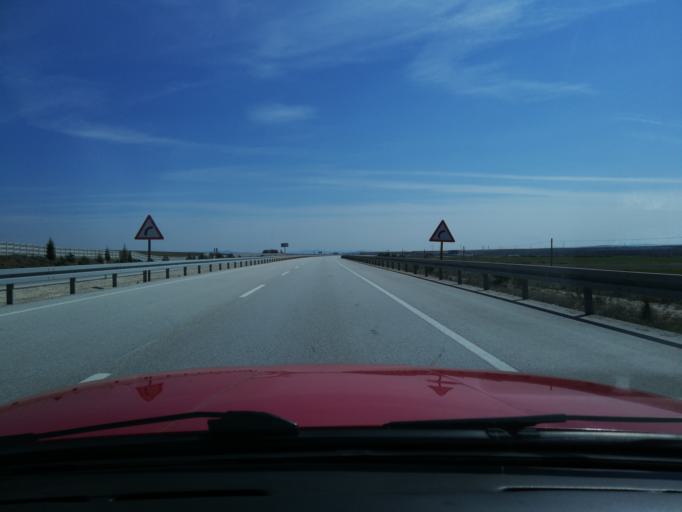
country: TR
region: Kuetahya
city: Altintas
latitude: 39.0872
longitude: 30.1936
